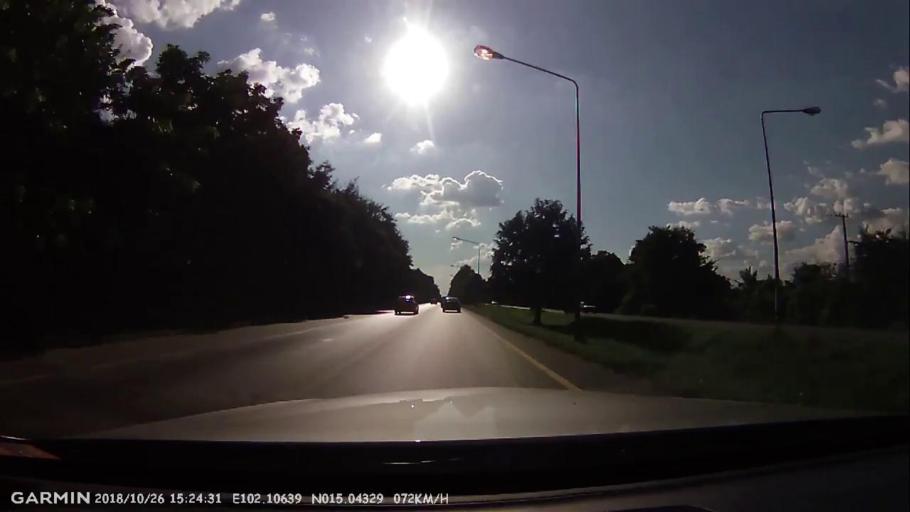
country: TH
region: Nakhon Ratchasima
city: Nakhon Ratchasima
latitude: 15.0433
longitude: 102.1065
